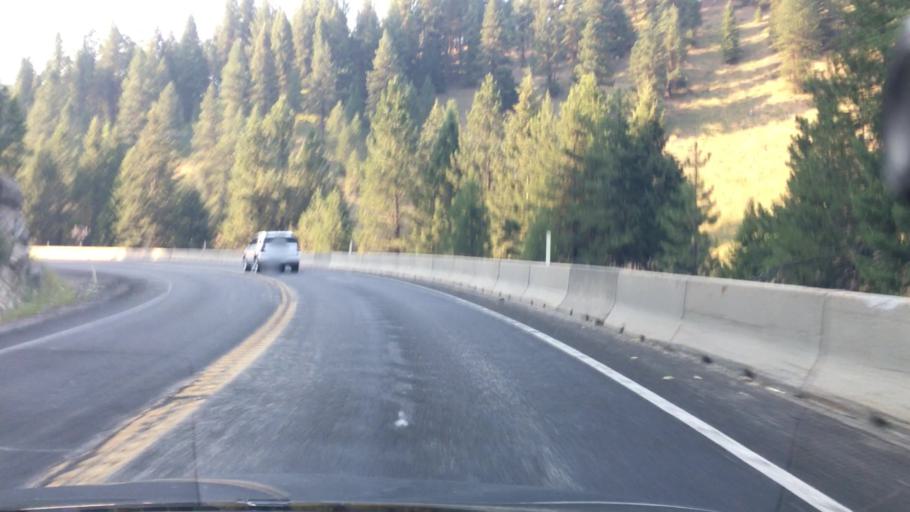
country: US
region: Idaho
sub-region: Valley County
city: Cascade
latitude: 44.2644
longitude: -116.0670
